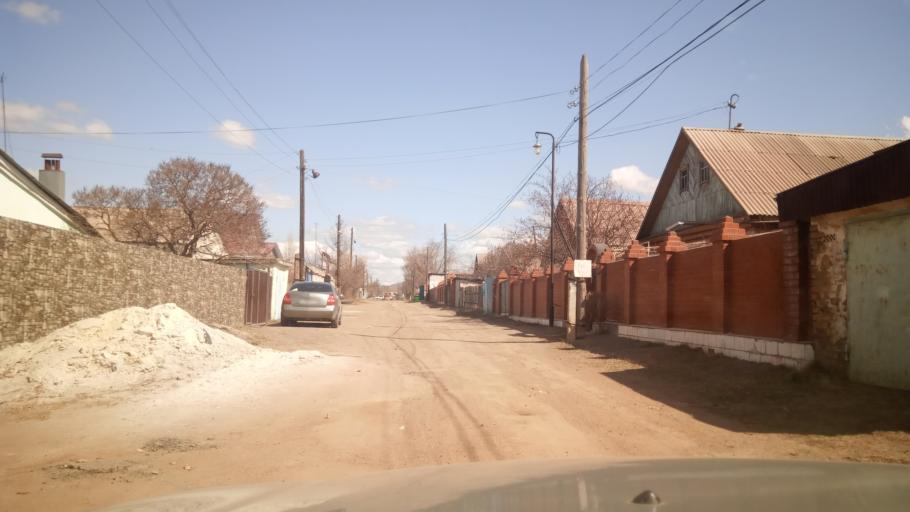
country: RU
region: Orenburg
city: Novotroitsk
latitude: 51.2065
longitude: 58.3157
